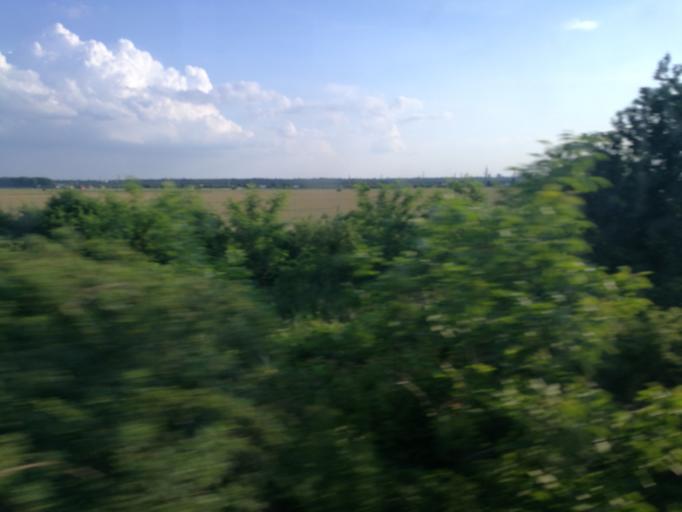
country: RO
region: Arges
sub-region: Comuna Calinesti
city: Vranesti
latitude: 44.8275
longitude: 25.0043
